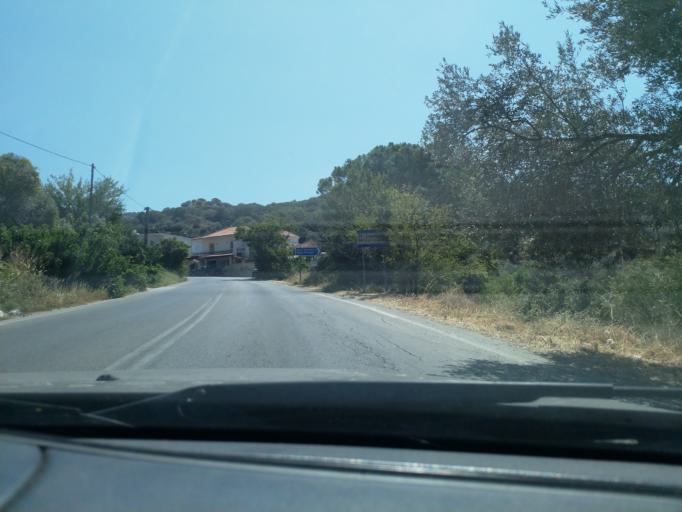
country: GR
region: Crete
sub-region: Nomos Rethymnis
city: Agia Foteini
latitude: 35.2193
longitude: 24.5006
